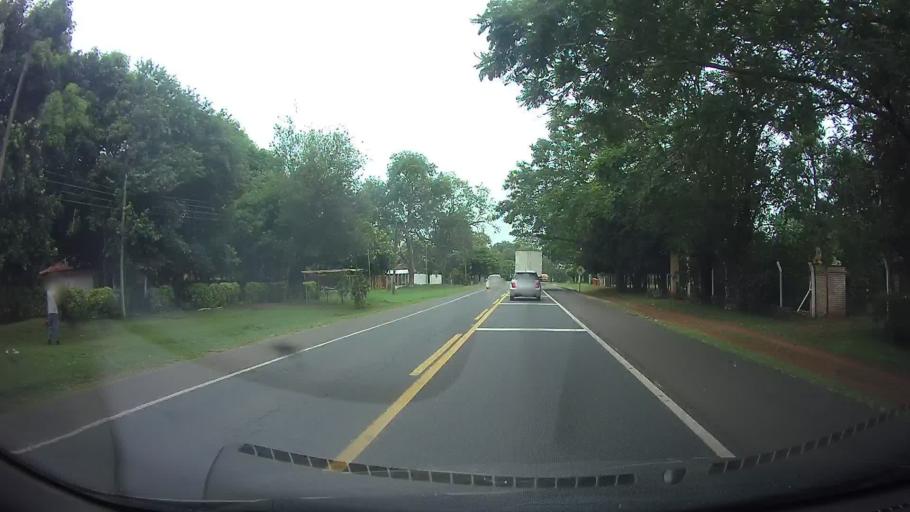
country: PY
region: Paraguari
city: Paraguari
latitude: -25.5978
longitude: -57.2067
